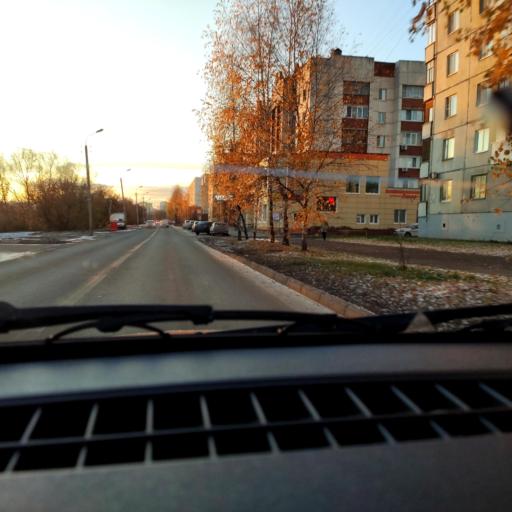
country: RU
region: Bashkortostan
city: Mikhaylovka
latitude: 54.7093
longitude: 55.8378
